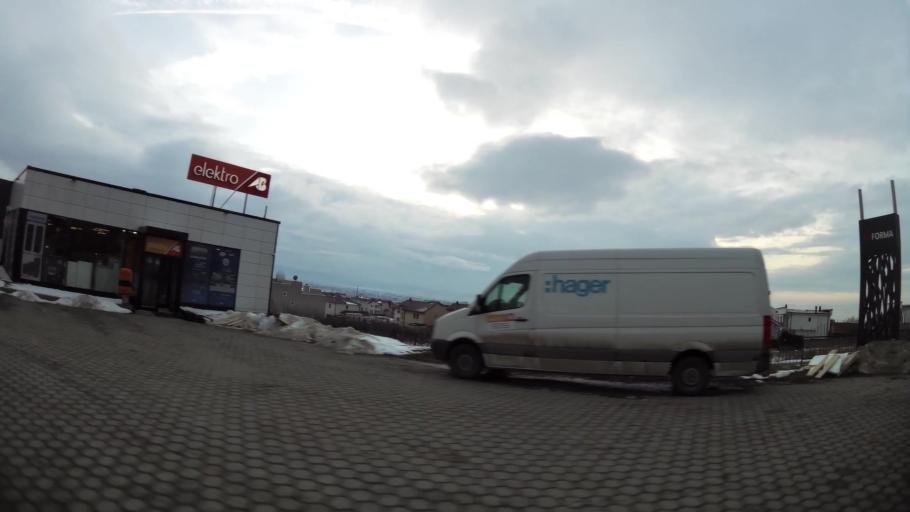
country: XK
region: Pristina
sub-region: Komuna e Prishtines
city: Pristina
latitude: 42.6221
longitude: 21.1621
